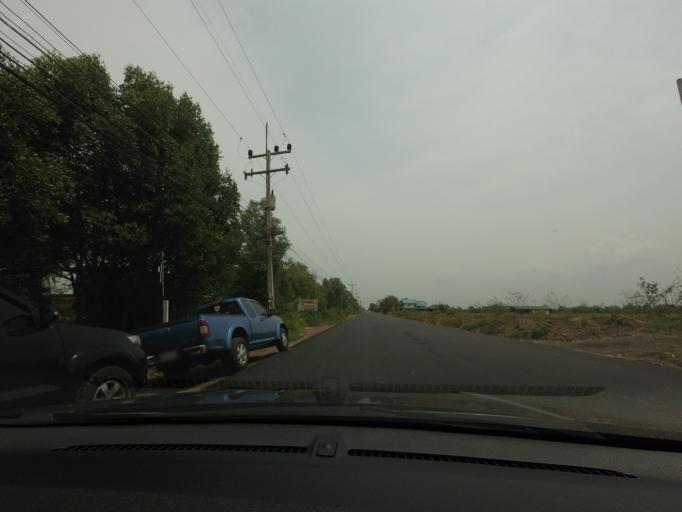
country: TH
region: Samut Songkhram
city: Amphawa
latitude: 13.3406
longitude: 99.9300
